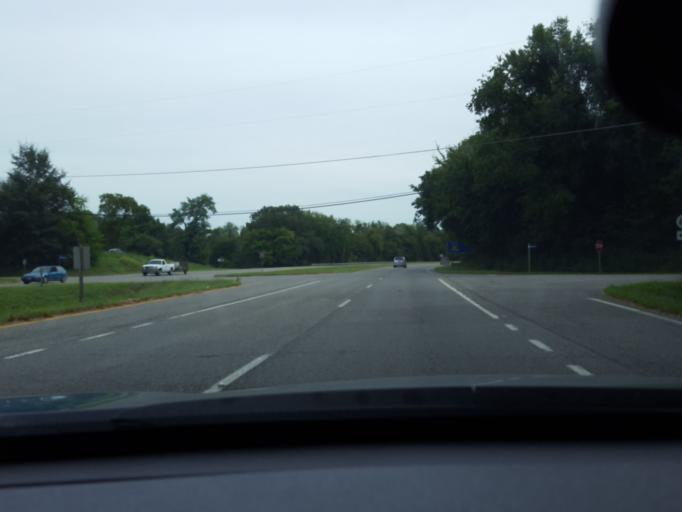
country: US
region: Virginia
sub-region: Caroline County
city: Bowling Green
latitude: 38.0507
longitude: -77.3412
